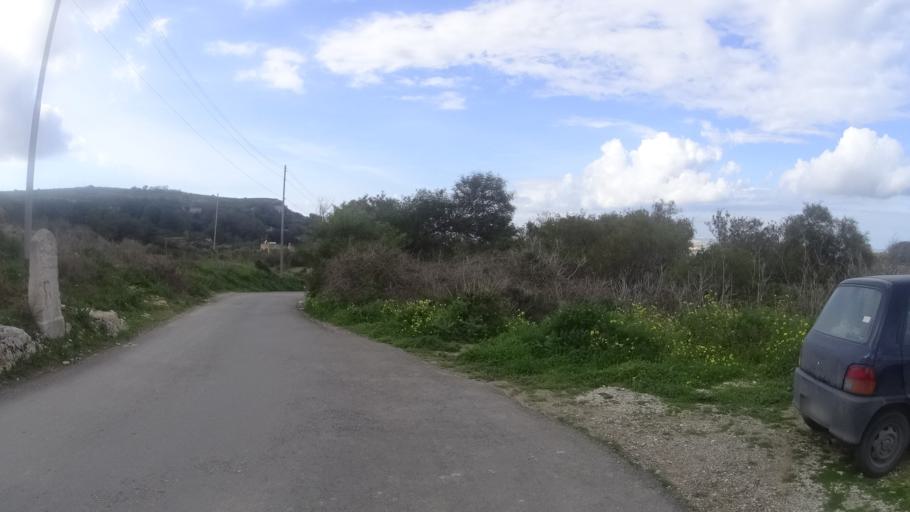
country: MT
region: L-Imgarr
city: Imgarr
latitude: 35.9028
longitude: 14.3785
